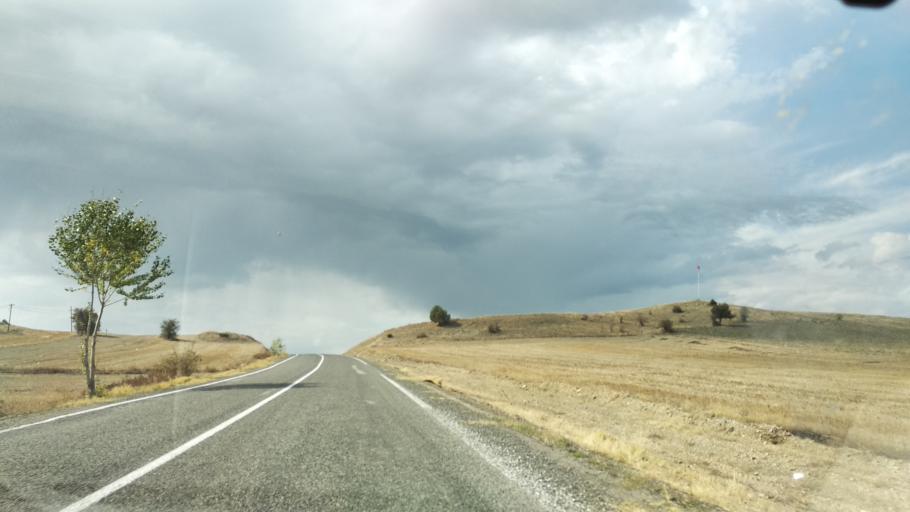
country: TR
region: Bolu
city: Seben
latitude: 40.3683
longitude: 31.5032
